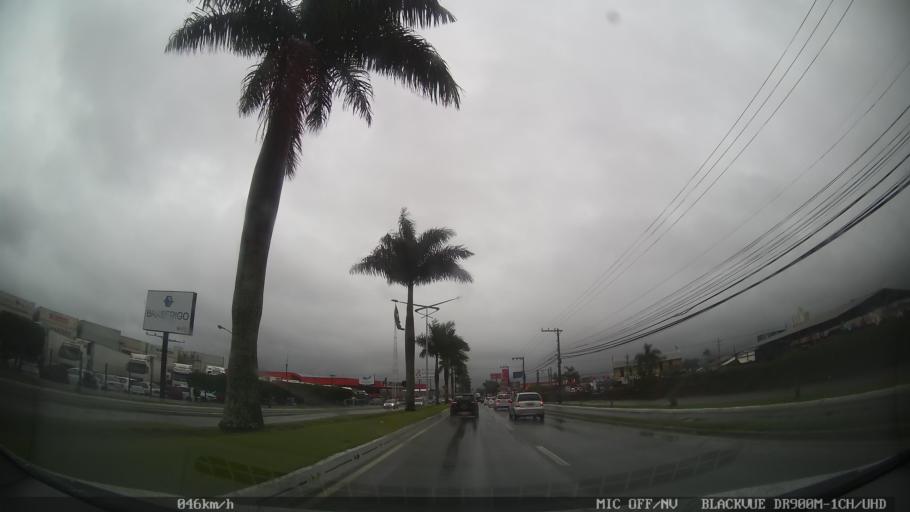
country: BR
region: Santa Catarina
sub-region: Itajai
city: Itajai
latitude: -26.9115
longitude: -48.6879
